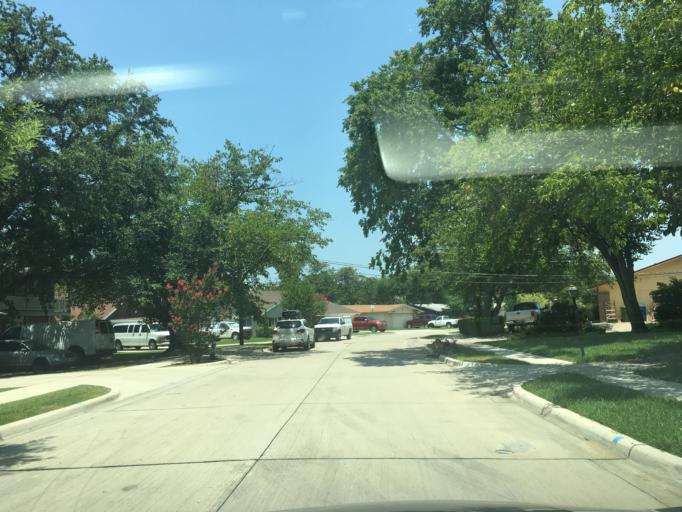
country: US
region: Texas
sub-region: Dallas County
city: Carrollton
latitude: 32.9469
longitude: -96.8767
